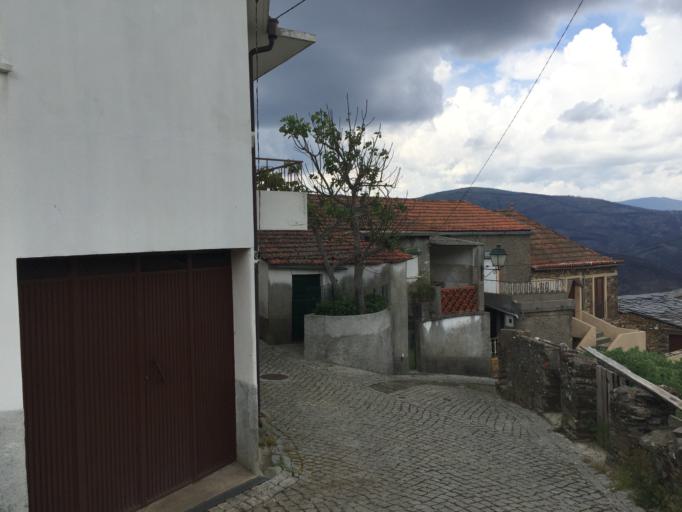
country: PT
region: Coimbra
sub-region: Pampilhosa da Serra
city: Pampilhosa da Serra
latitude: 40.1492
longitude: -7.9242
